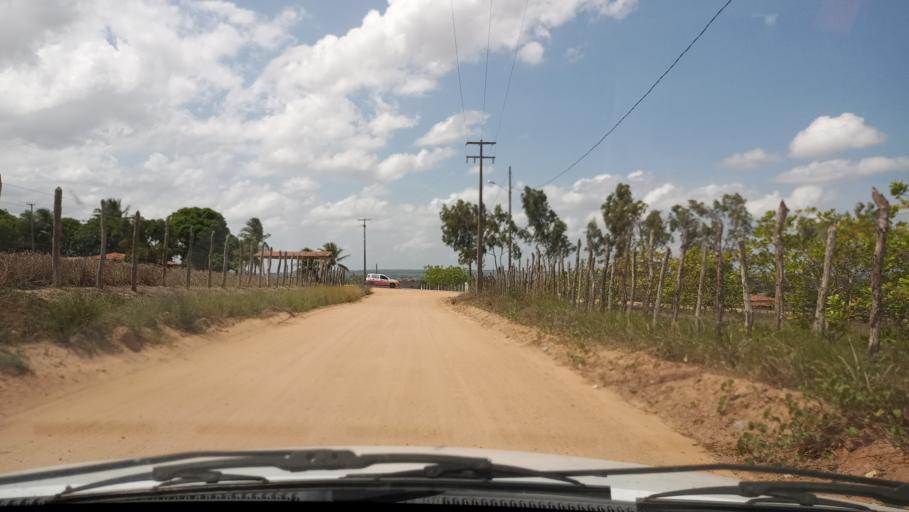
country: BR
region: Rio Grande do Norte
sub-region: Goianinha
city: Goianinha
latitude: -6.3408
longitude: -35.3262
